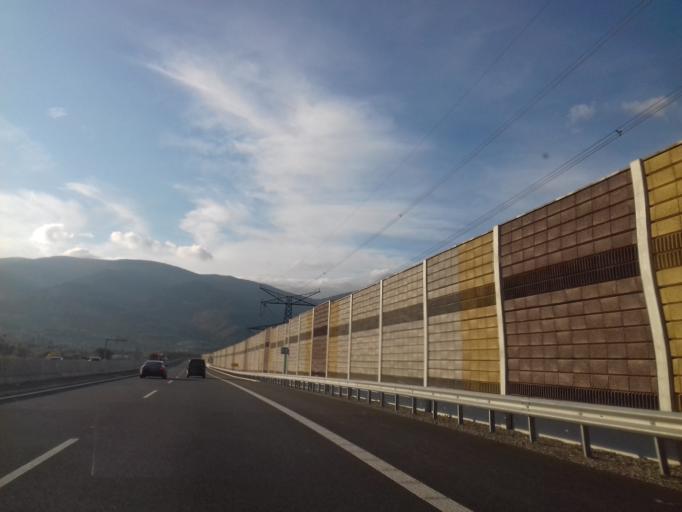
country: SK
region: Zilinsky
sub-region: Okres Zilina
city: Vrutky
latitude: 49.1215
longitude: 18.9317
